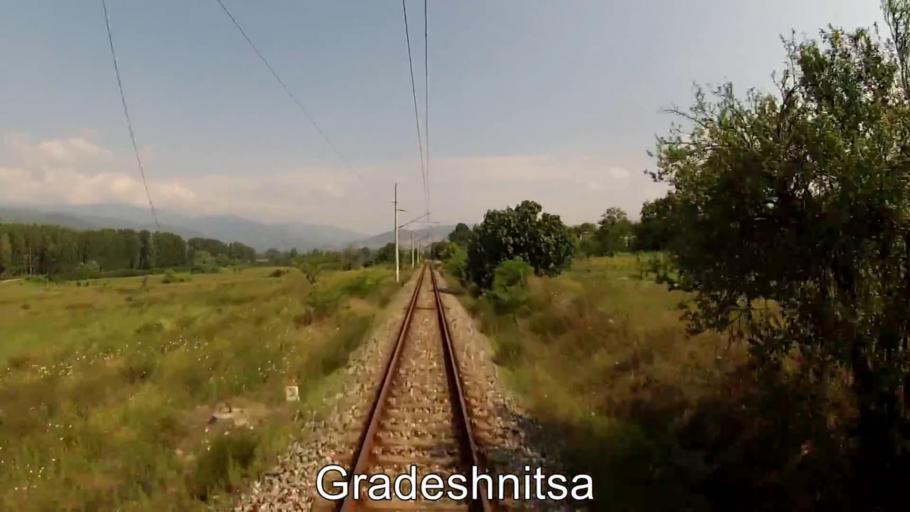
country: BG
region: Blagoevgrad
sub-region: Obshtina Strumyani
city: Strumyani
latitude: 41.6563
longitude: 23.1788
